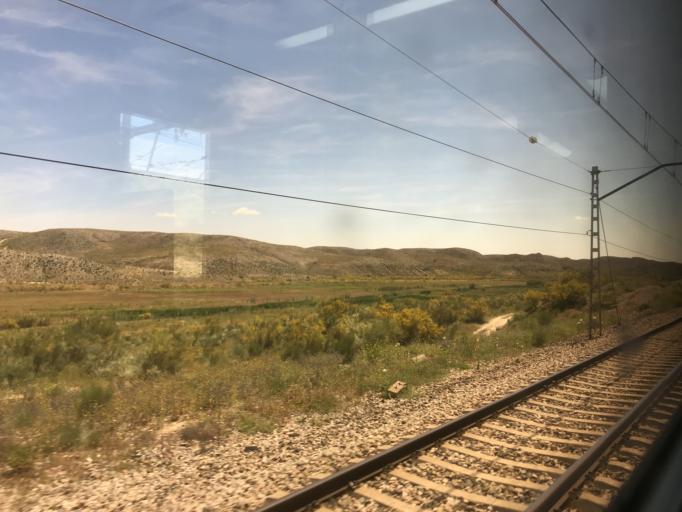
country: ES
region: Madrid
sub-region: Provincia de Madrid
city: Ciempozuelos
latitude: 40.1737
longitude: -3.6257
